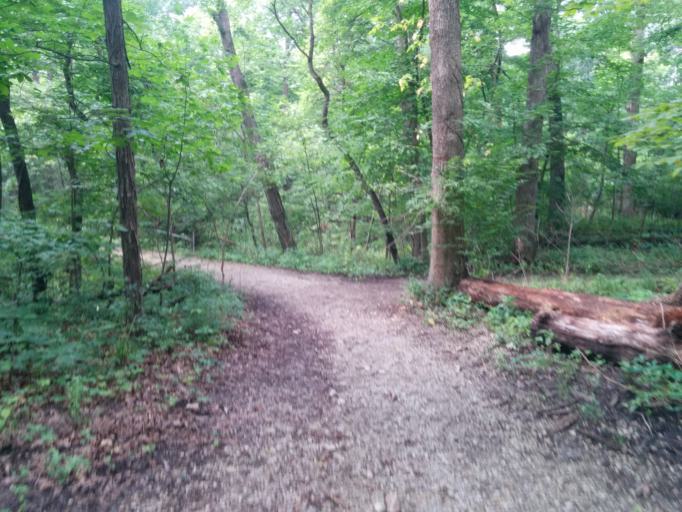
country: US
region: Illinois
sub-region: Cook County
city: Palos Park
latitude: 41.6762
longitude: -87.8316
